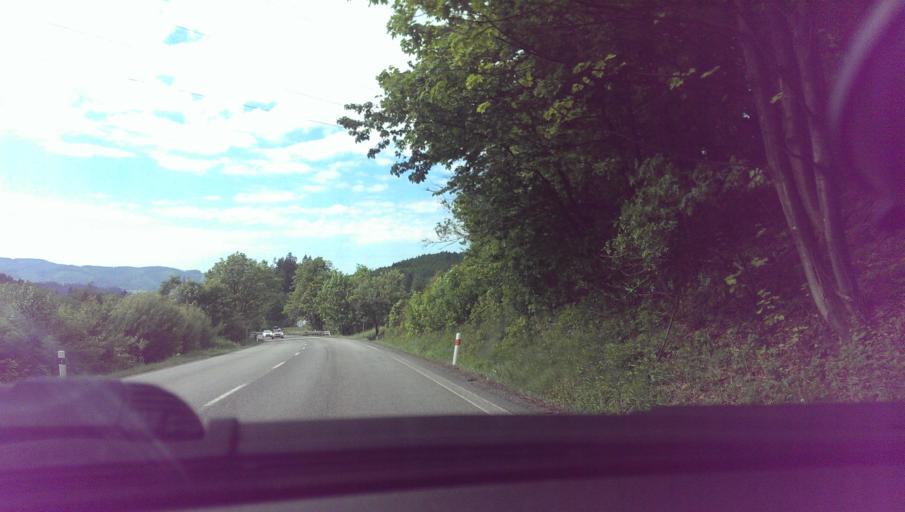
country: CZ
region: Zlin
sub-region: Okres Vsetin
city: Roznov pod Radhostem
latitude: 49.4904
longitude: 18.1707
